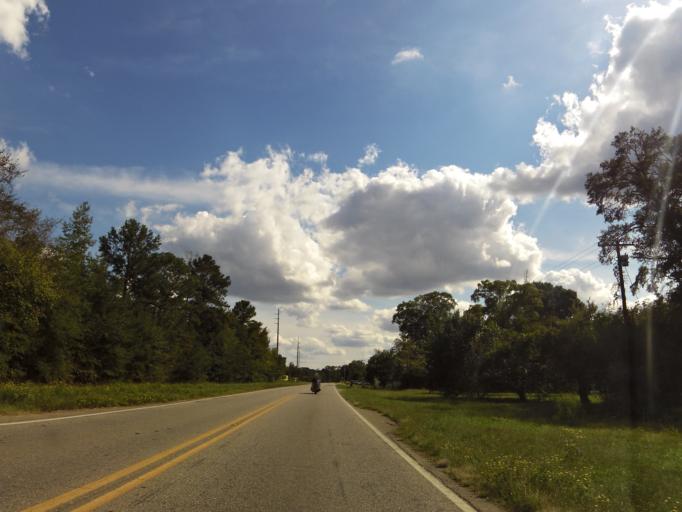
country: US
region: Alabama
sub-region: Dallas County
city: Selmont-West Selmont
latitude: 32.3292
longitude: -86.9932
